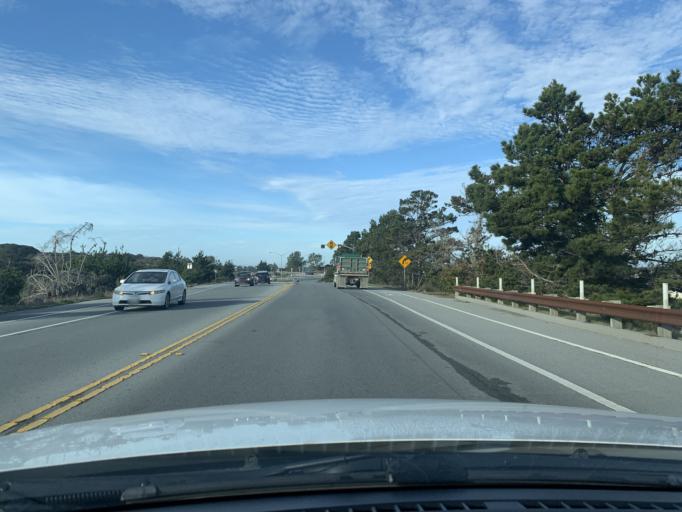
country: US
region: California
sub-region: Monterey County
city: Marina
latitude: 36.6621
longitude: -121.7886
